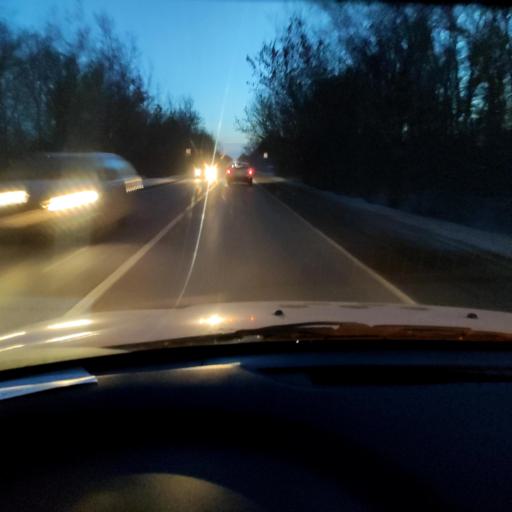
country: RU
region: Samara
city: Tol'yatti
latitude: 53.5527
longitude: 49.3938
